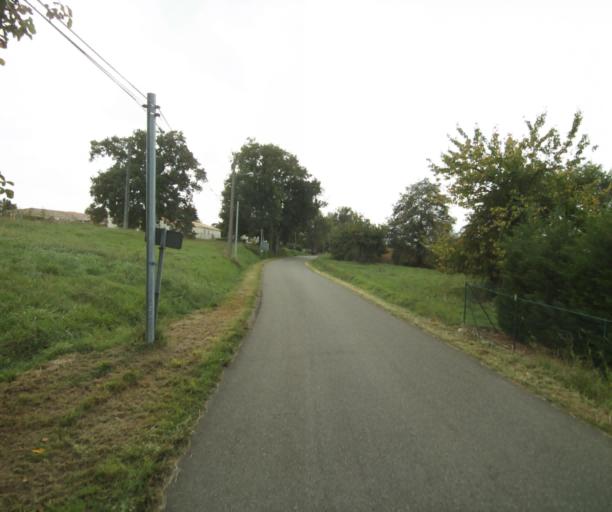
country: FR
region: Midi-Pyrenees
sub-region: Departement du Gers
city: Eauze
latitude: 43.8560
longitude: 0.0917
